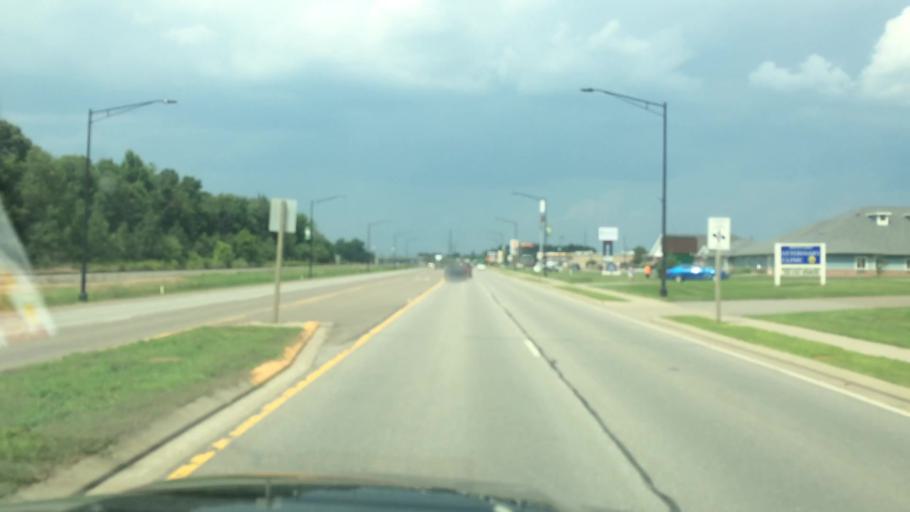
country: US
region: Wisconsin
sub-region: Clark County
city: Colby
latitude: 44.9255
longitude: -90.3155
